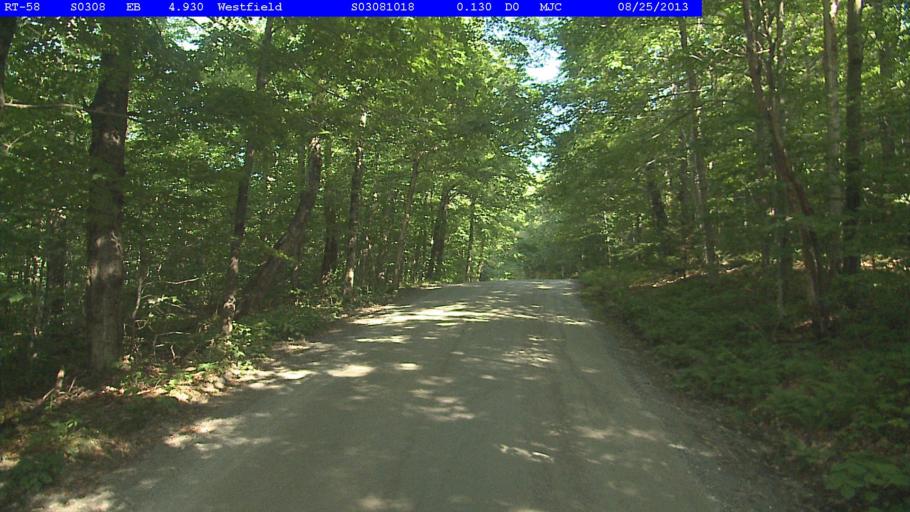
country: US
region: Vermont
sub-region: Franklin County
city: Richford
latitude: 44.8407
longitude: -72.5308
